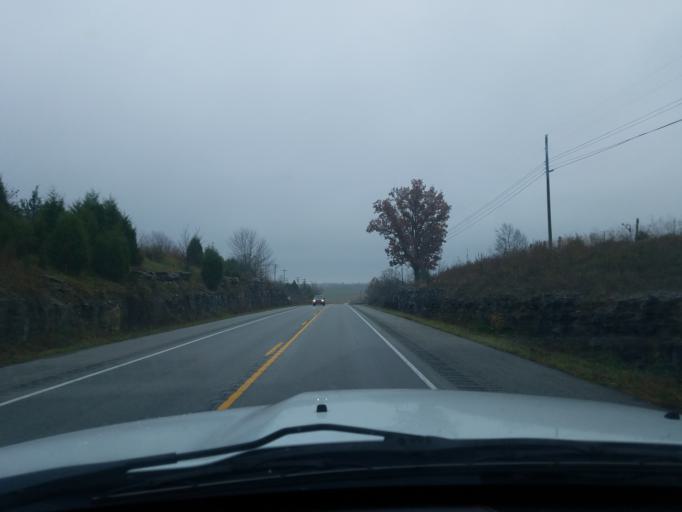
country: US
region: Kentucky
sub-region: Green County
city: Greensburg
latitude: 37.4002
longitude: -85.4744
